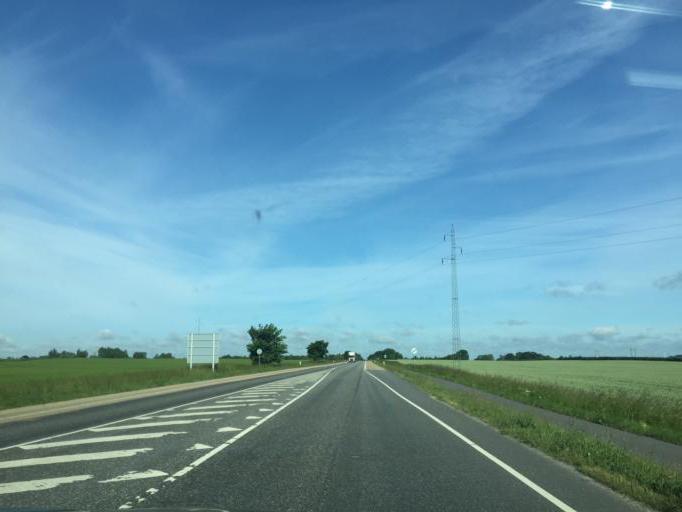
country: DK
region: South Denmark
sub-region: Middelfart Kommune
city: Strib
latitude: 55.4889
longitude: 9.8056
